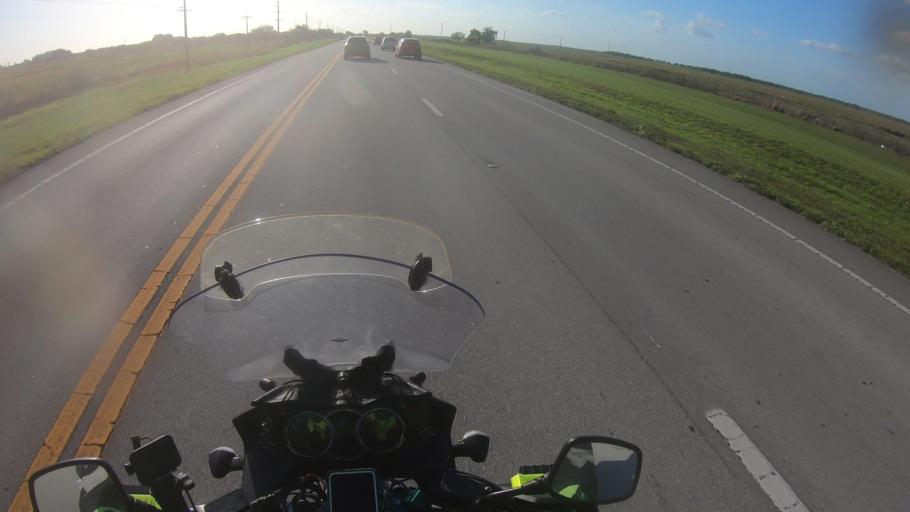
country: US
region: Florida
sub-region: DeSoto County
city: Southeast Arcadia
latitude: 27.2099
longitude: -81.7237
